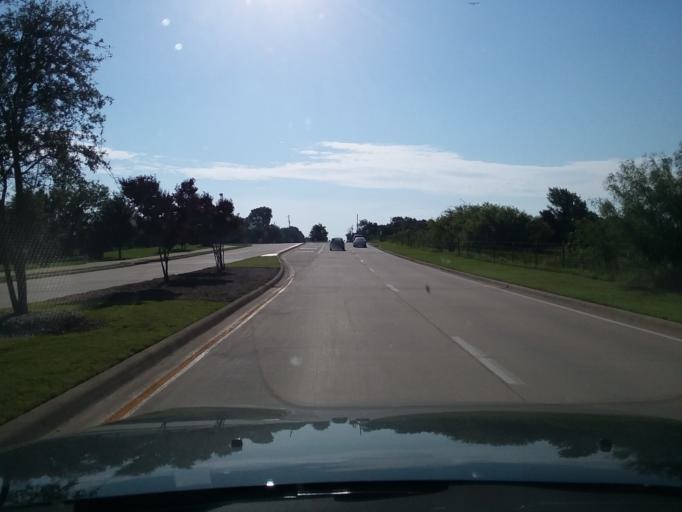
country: US
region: Texas
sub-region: Denton County
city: Highland Village
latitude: 33.0664
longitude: -97.0733
